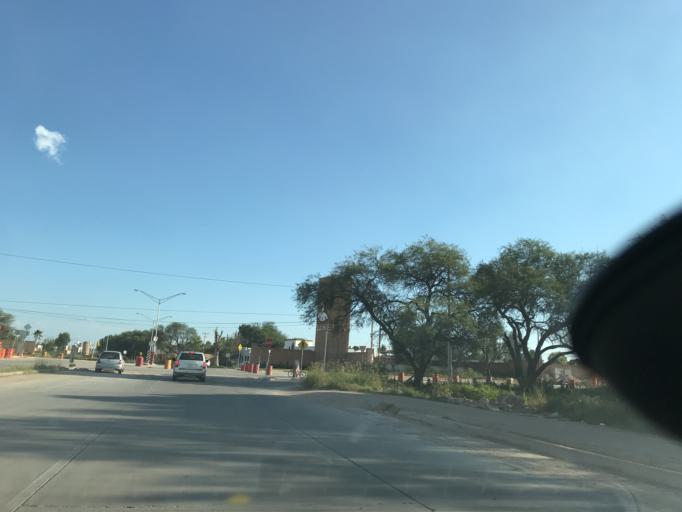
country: MX
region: Aguascalientes
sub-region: Aguascalientes
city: Pocitos
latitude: 21.9072
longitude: -102.3311
